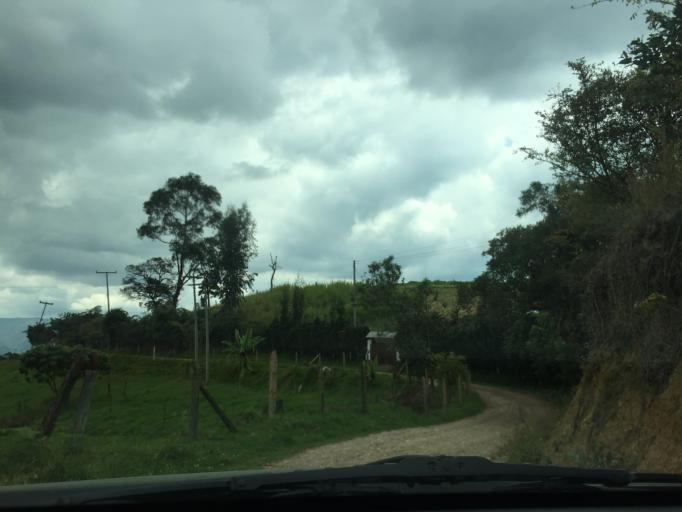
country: CO
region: Cundinamarca
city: Zipaquira
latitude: 5.0550
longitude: -74.0148
